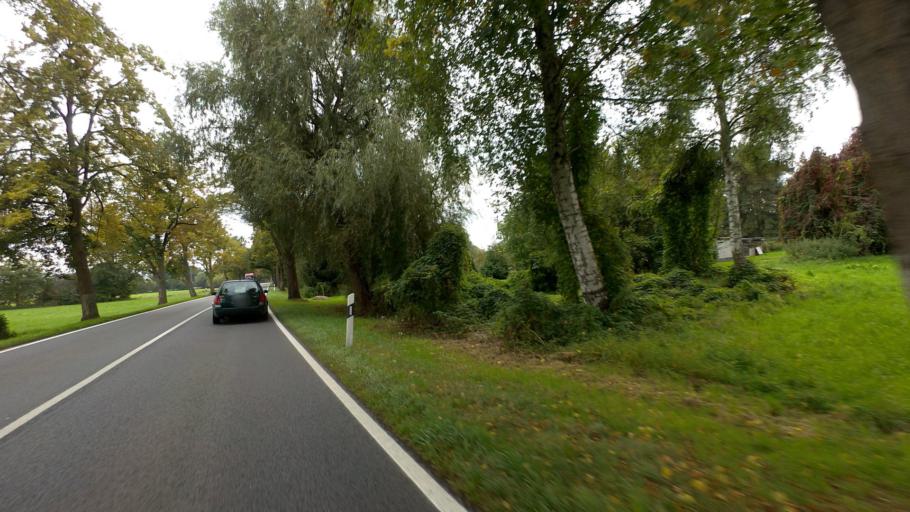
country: DE
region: Brandenburg
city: Golssen
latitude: 51.9681
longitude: 13.6143
